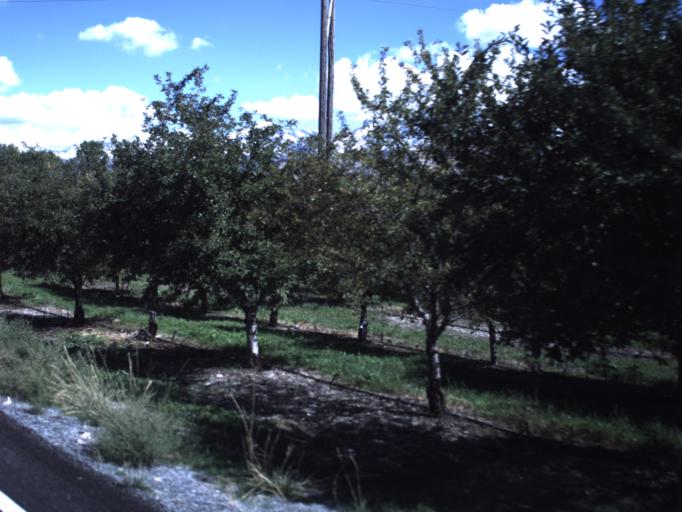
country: US
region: Utah
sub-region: Utah County
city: Santaquin
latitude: 40.0140
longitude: -111.7987
